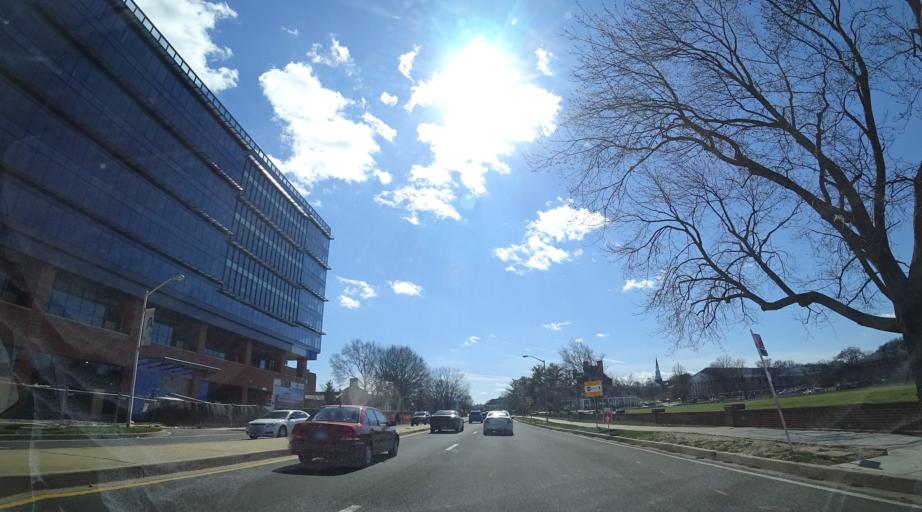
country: US
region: Maryland
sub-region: Prince George's County
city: College Park
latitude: 38.9876
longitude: -76.9359
